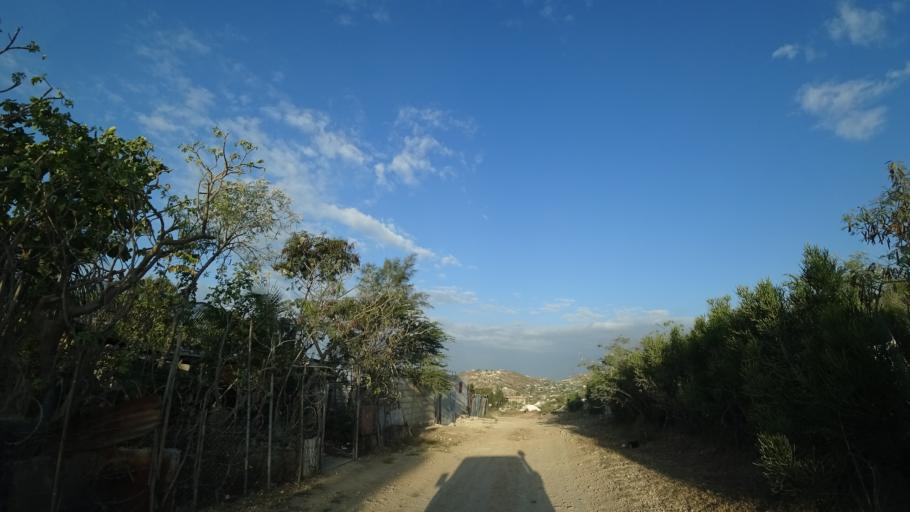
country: HT
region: Ouest
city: Croix des Bouquets
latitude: 18.6675
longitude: -72.2792
